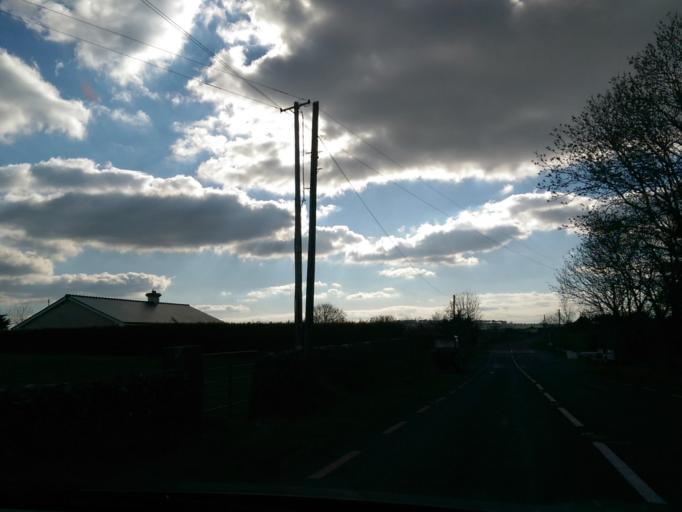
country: IE
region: Connaught
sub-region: County Galway
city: Loughrea
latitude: 53.1991
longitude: -8.4422
